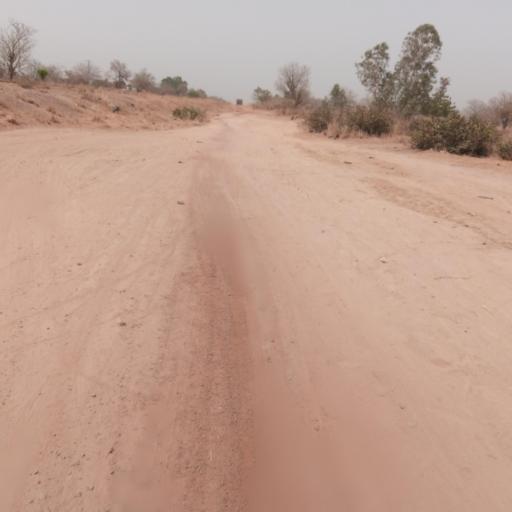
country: BF
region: Centre
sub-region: Kadiogo Province
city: Ouagadougou
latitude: 12.3433
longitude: -1.6776
